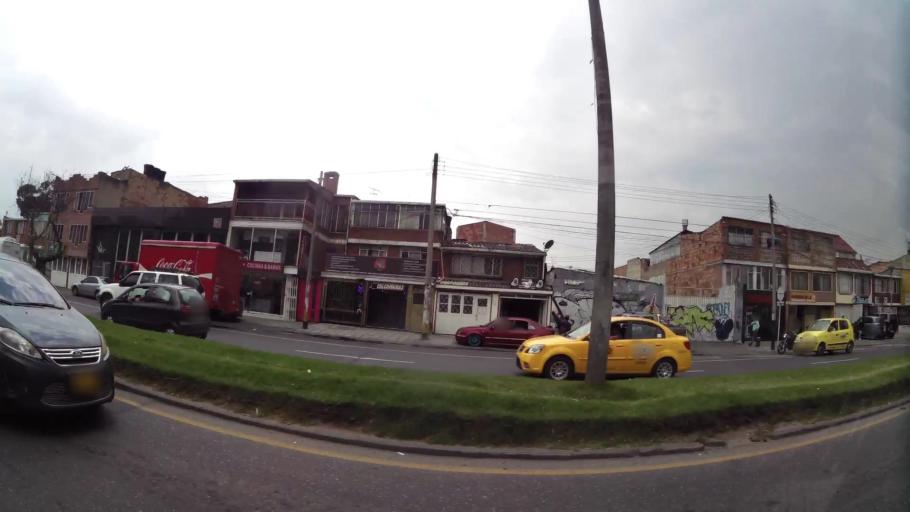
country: CO
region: Bogota D.C.
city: Bogota
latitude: 4.6073
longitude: -74.1186
